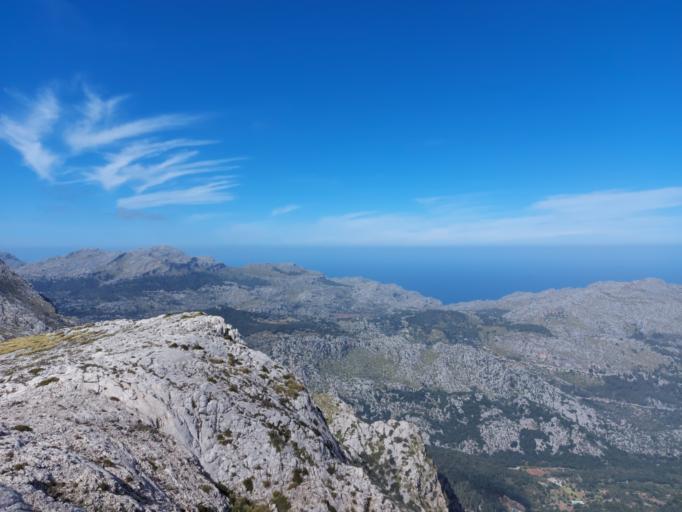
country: ES
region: Balearic Islands
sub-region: Illes Balears
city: Campanet
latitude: 39.8439
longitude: 2.9457
